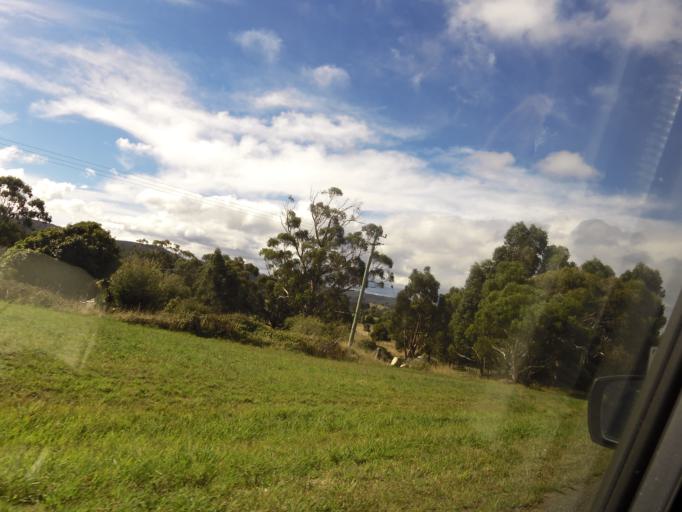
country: AU
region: Tasmania
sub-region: Kingborough
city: Kingston
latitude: -42.9723
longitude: 147.2748
